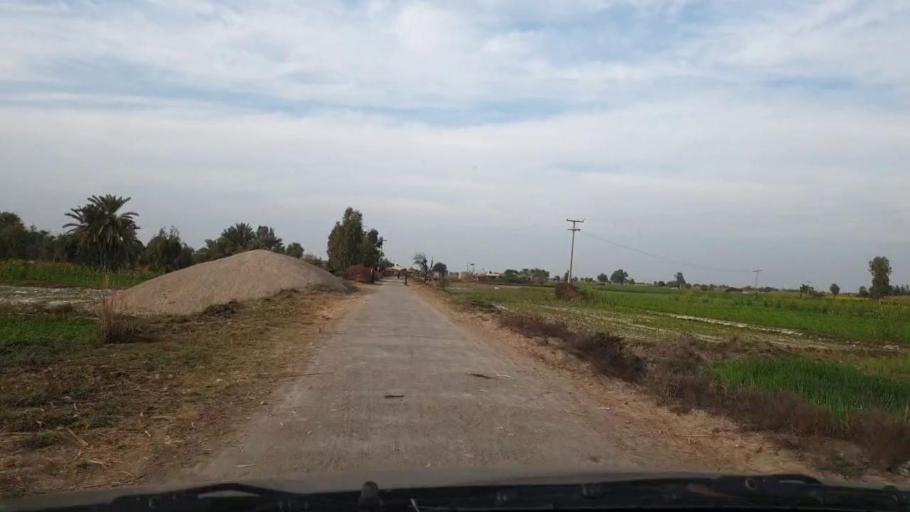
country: PK
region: Sindh
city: Khadro
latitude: 26.1652
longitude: 68.7263
